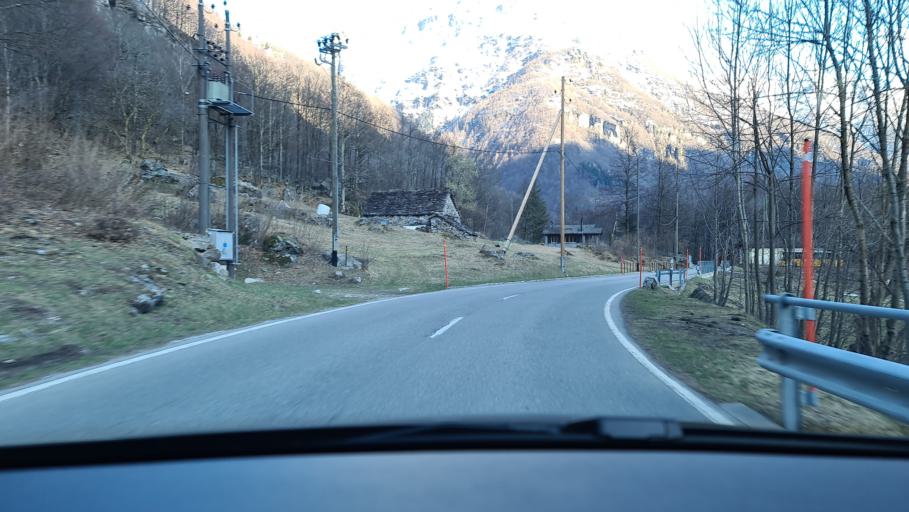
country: CH
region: Ticino
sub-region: Locarno District
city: Lavertezzo
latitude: 46.3476
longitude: 8.7926
